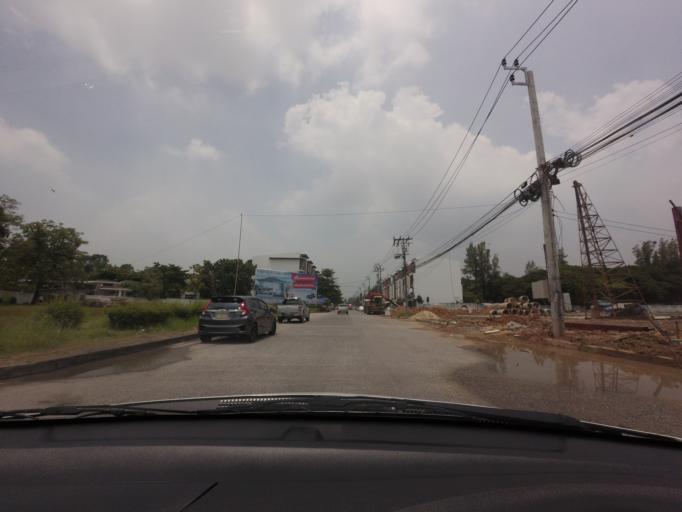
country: TH
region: Bangkok
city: Bang Na
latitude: 13.6629
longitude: 100.6951
